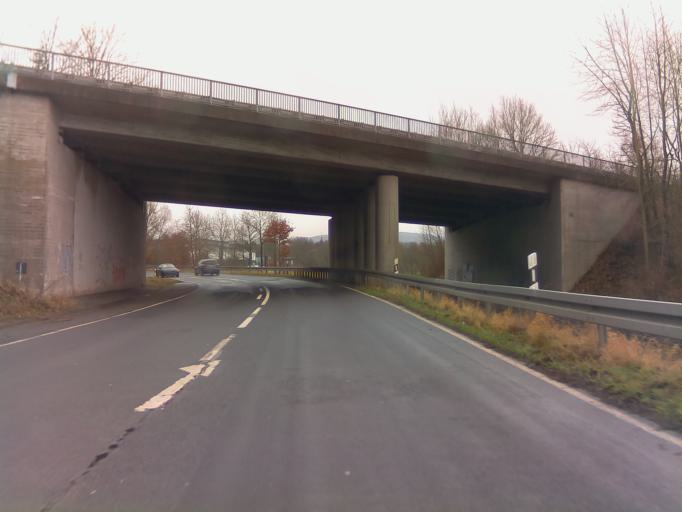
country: DE
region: Hesse
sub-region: Regierungsbezirk Kassel
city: Eichenzell
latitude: 50.5031
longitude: 9.6848
